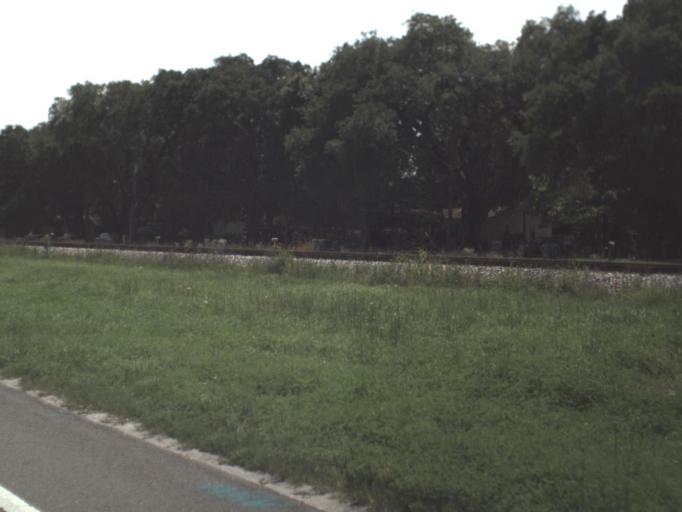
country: US
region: Florida
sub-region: Nassau County
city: Yulee
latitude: 30.4889
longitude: -81.6255
